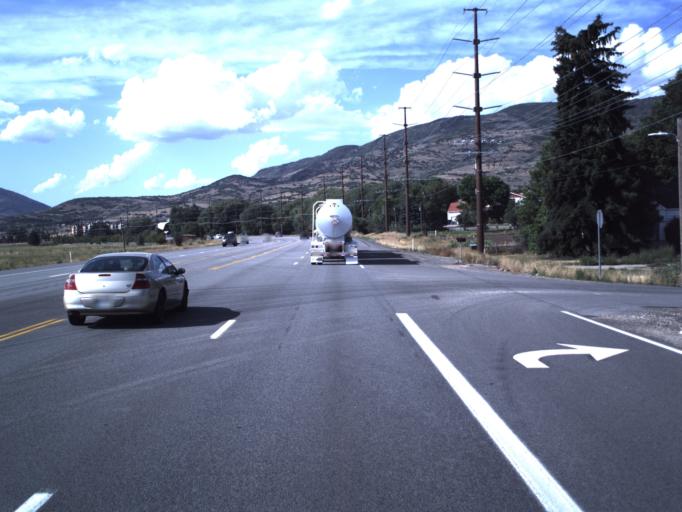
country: US
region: Utah
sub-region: Wasatch County
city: Heber
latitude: 40.5307
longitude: -111.4093
